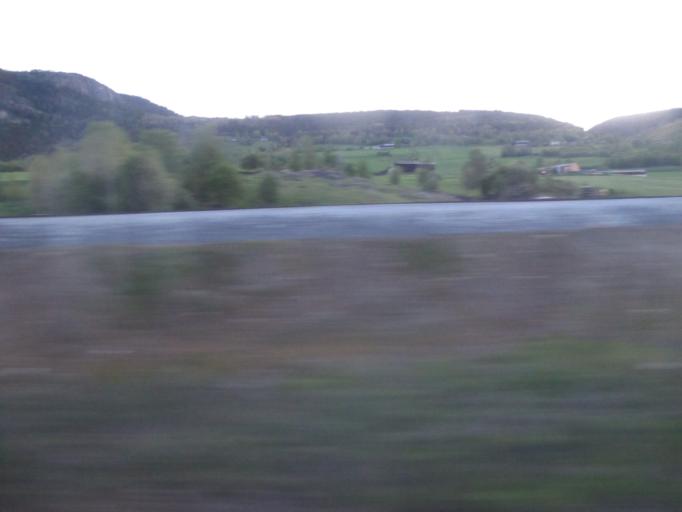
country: NO
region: Oppland
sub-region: Sor-Fron
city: Hundorp
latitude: 61.5695
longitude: 9.8970
